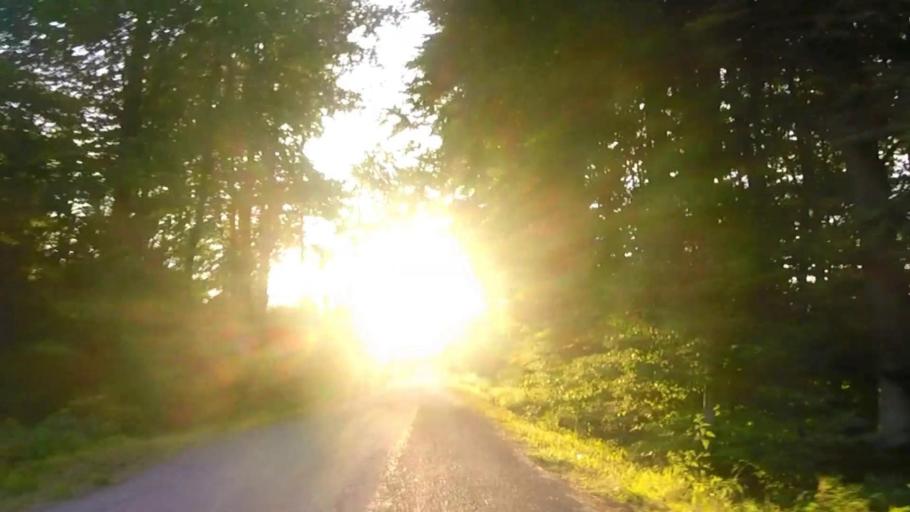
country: DE
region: Baden-Wuerttemberg
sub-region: Regierungsbezirk Stuttgart
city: Aspach
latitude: 49.0136
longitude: 9.4023
